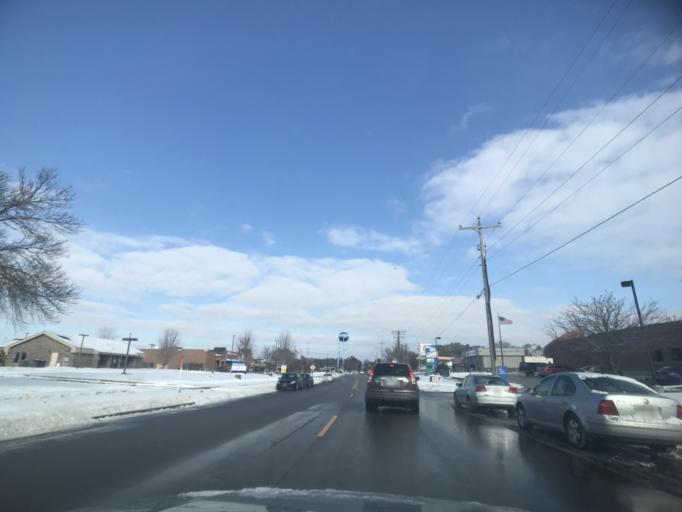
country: US
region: Wisconsin
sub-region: Brown County
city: De Pere
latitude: 44.4489
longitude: -88.0845
